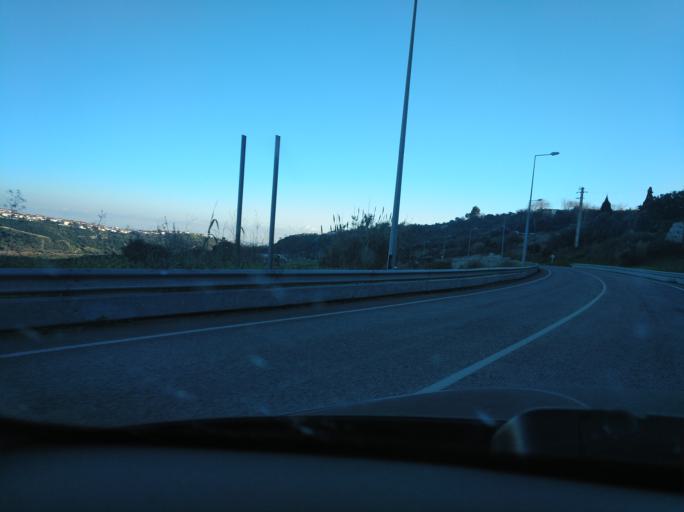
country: PT
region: Lisbon
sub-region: Loures
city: Unhos
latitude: 38.8264
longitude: -9.1264
